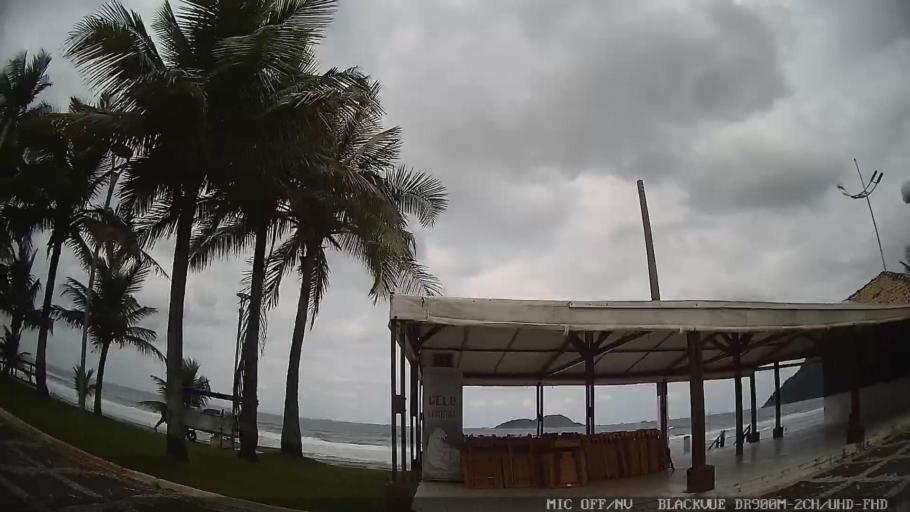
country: BR
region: Sao Paulo
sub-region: Guaruja
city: Guaruja
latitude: -24.0148
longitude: -46.2748
